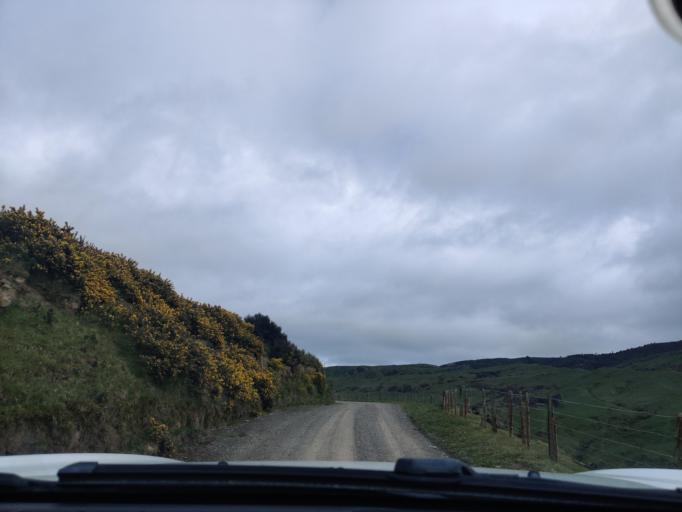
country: NZ
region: Manawatu-Wanganui
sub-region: Palmerston North City
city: Palmerston North
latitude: -40.2857
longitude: 175.8637
